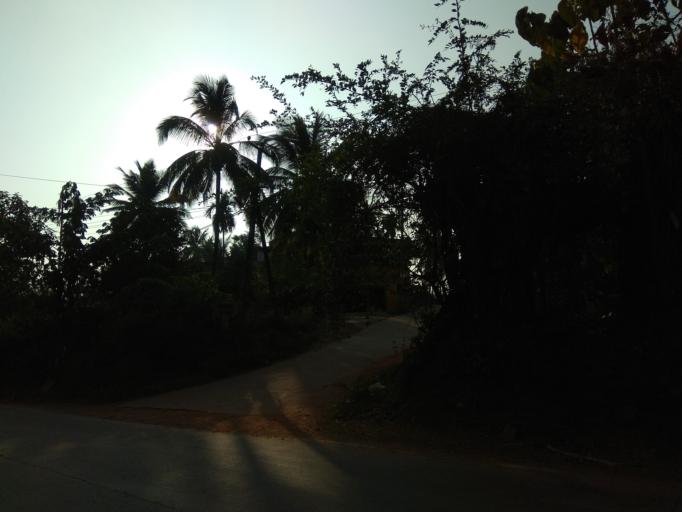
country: IN
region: Karnataka
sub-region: Dakshina Kannada
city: Mangalore
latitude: 12.9126
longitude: 74.8550
